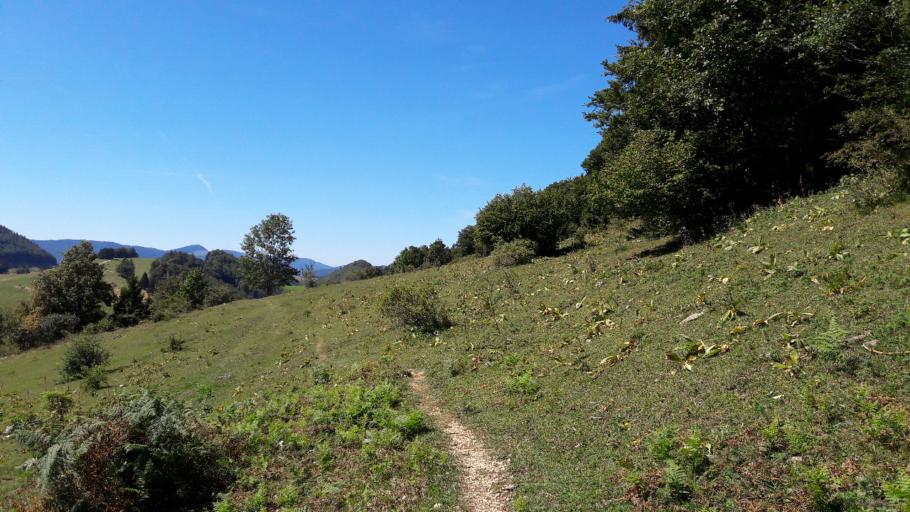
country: CH
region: Solothurn
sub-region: Bezirk Thal
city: Welschenrohr
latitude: 47.3157
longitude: 7.5715
